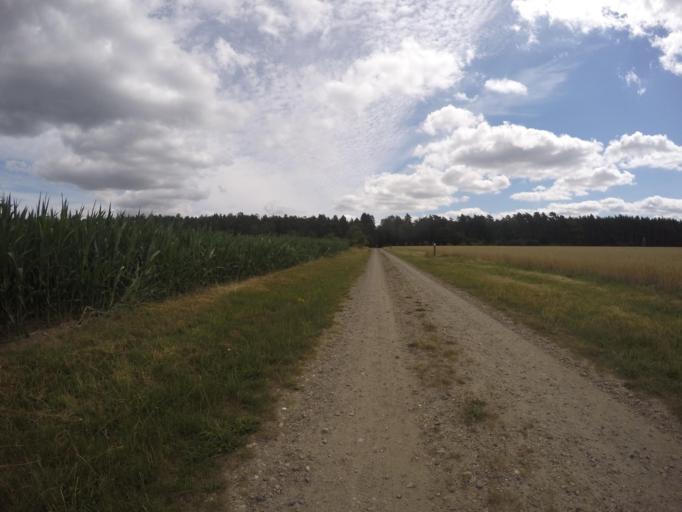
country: DE
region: Lower Saxony
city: Thomasburg
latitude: 53.2505
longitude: 10.6610
